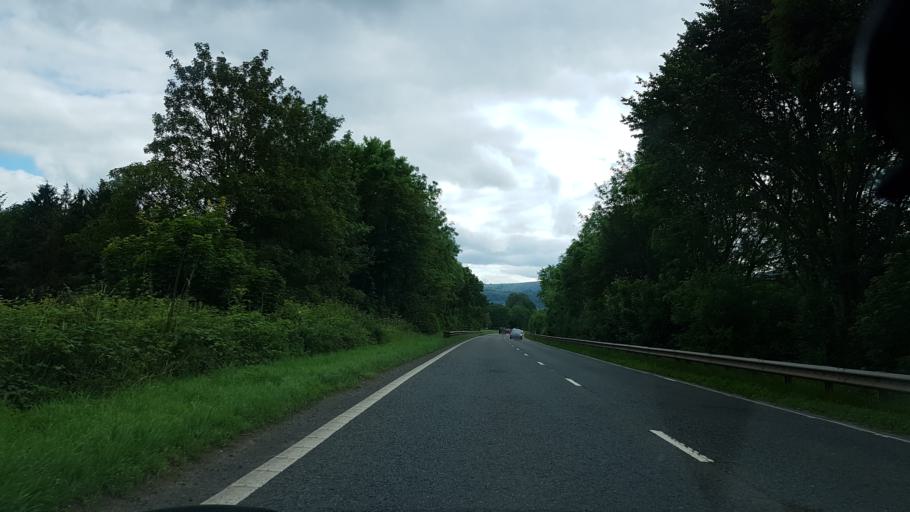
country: GB
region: Wales
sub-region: Monmouthshire
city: Abergavenny
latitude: 51.8297
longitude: -3.0019
